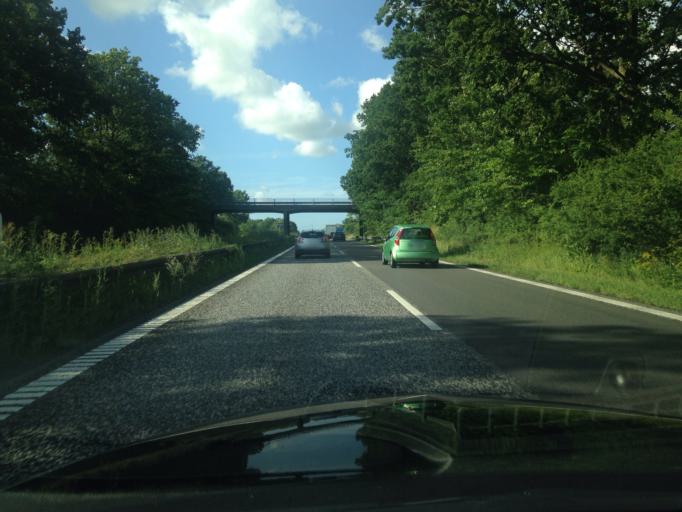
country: DK
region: Capital Region
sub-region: Horsholm Kommune
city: Horsholm
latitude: 55.8918
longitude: 12.4766
